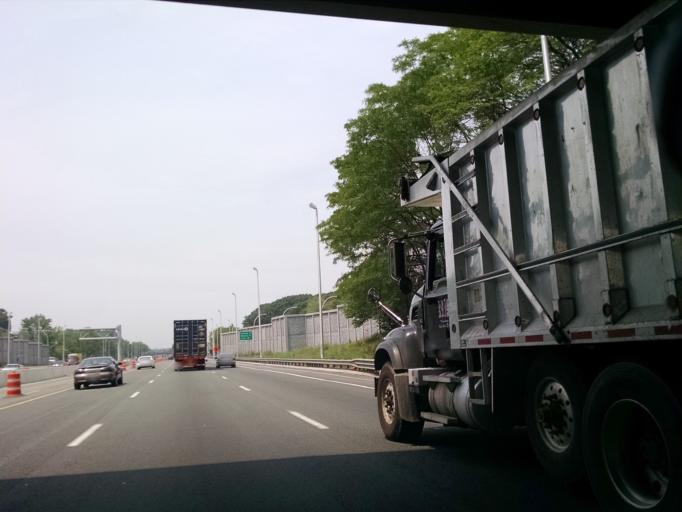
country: US
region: New York
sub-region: Richmond County
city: Bloomfield
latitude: 40.6082
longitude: -74.1323
